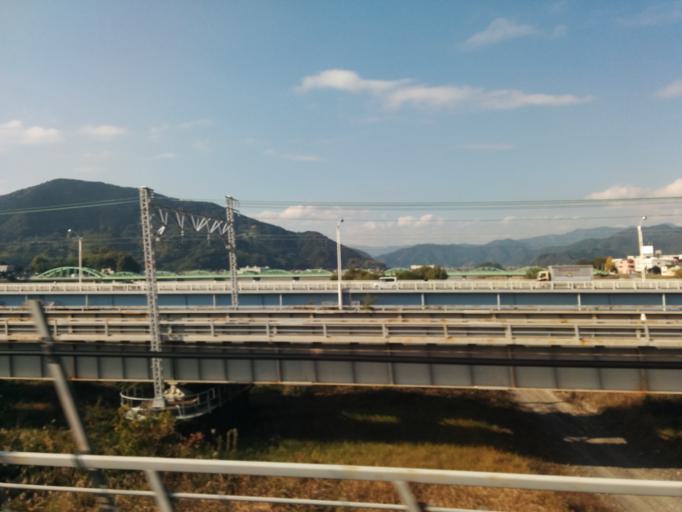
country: JP
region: Shizuoka
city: Shizuoka-shi
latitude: 34.9580
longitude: 138.3727
